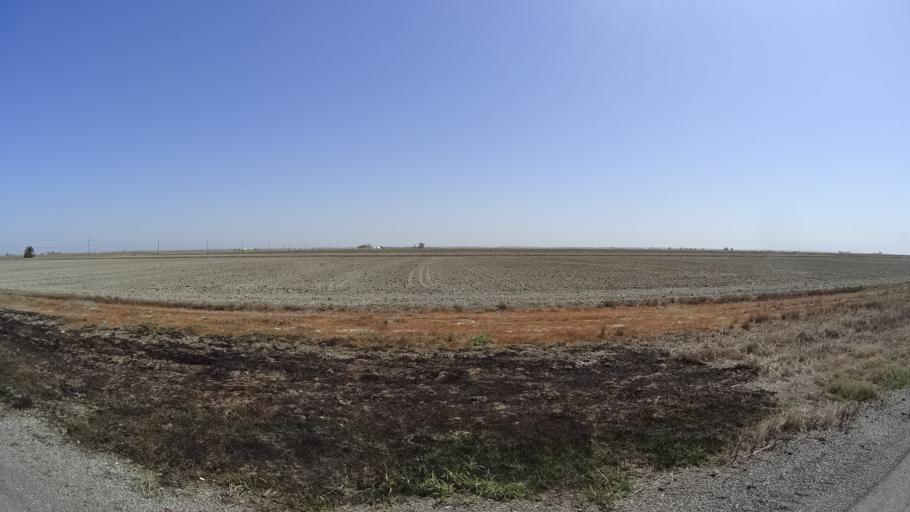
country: US
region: California
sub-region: Glenn County
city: Willows
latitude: 39.5198
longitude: -122.1027
